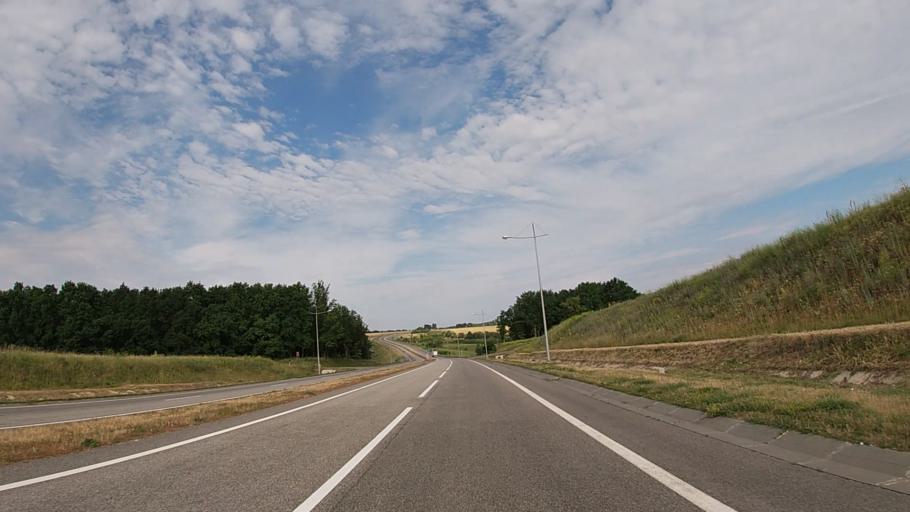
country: RU
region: Belgorod
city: Tomarovka
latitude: 50.7069
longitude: 36.2093
